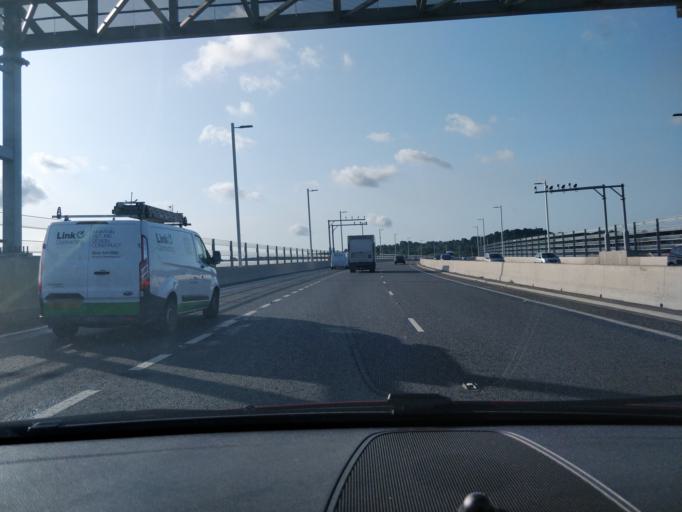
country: GB
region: England
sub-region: Borough of Halton
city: Runcorn
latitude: 53.3477
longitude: -2.7037
